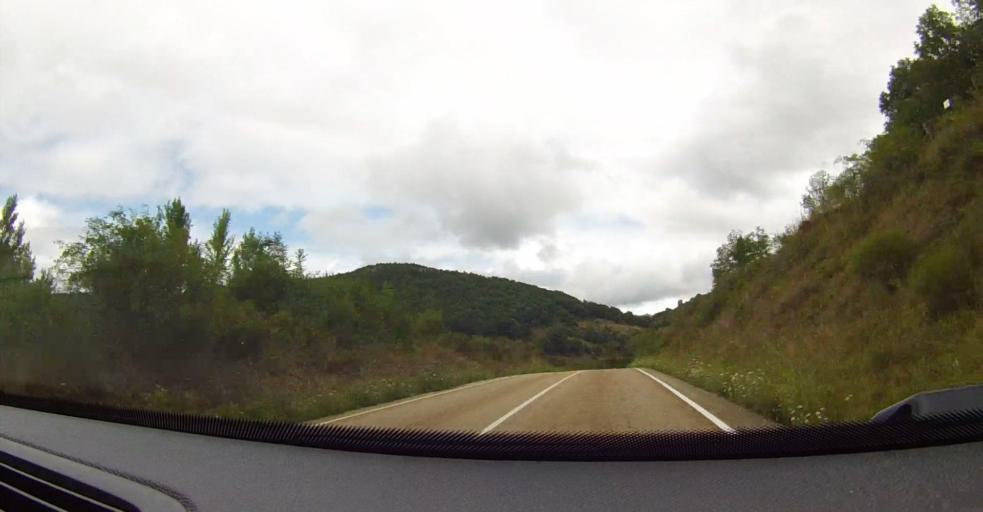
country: ES
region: Castille and Leon
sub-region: Provincia de Leon
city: Reyero
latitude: 42.9432
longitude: -5.2533
